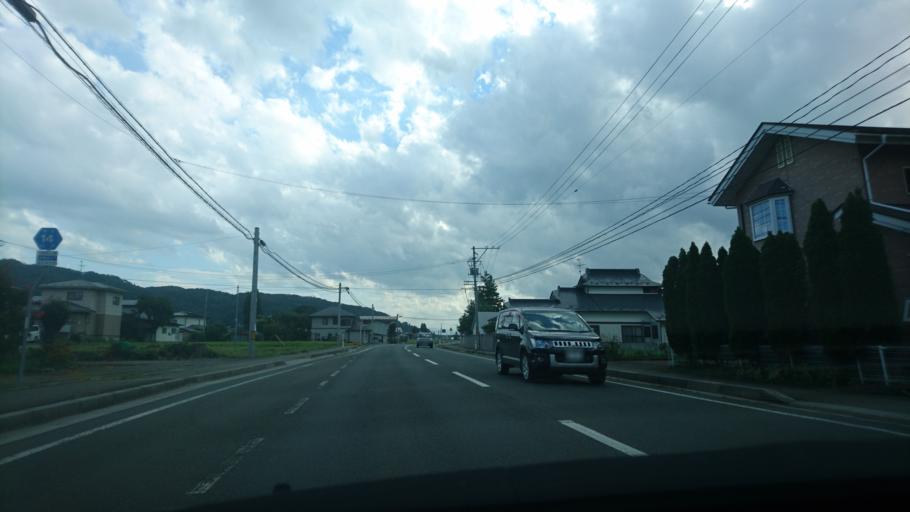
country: JP
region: Iwate
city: Kitakami
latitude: 39.2871
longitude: 141.1393
